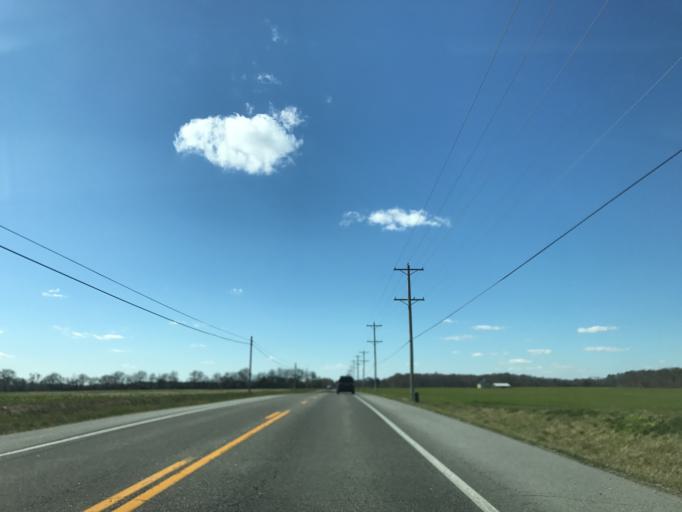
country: US
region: Maryland
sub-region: Kent County
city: Chestertown
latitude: 39.2202
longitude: -76.1486
